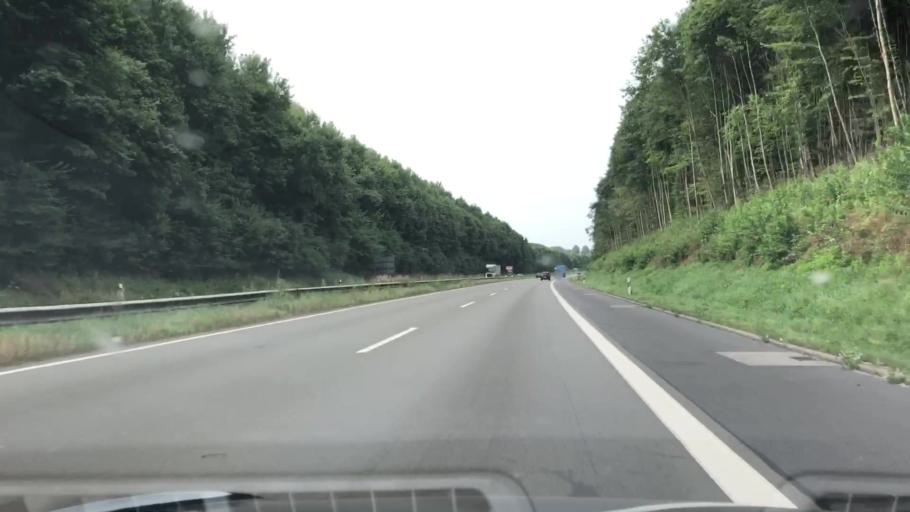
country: DE
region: Lower Saxony
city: Seevetal
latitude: 53.4168
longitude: 9.9242
